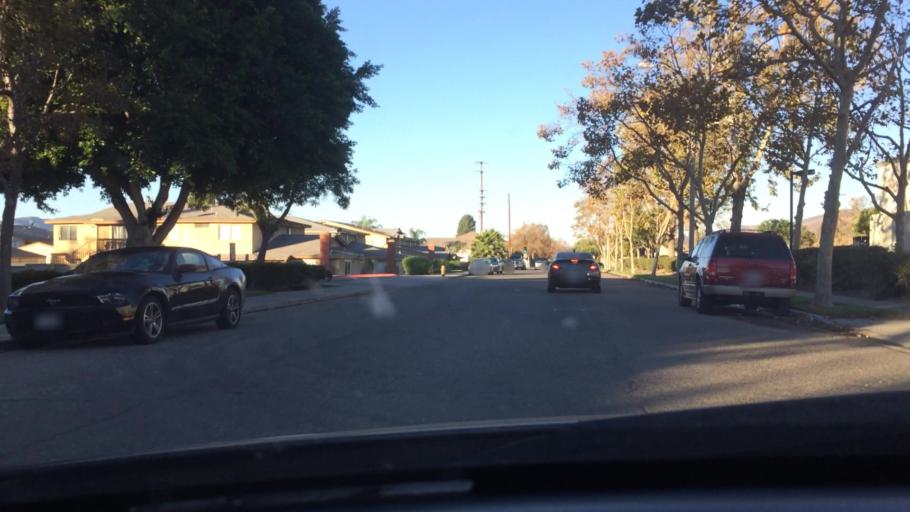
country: US
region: California
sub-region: Ventura County
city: Fillmore
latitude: 34.3946
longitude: -118.9158
